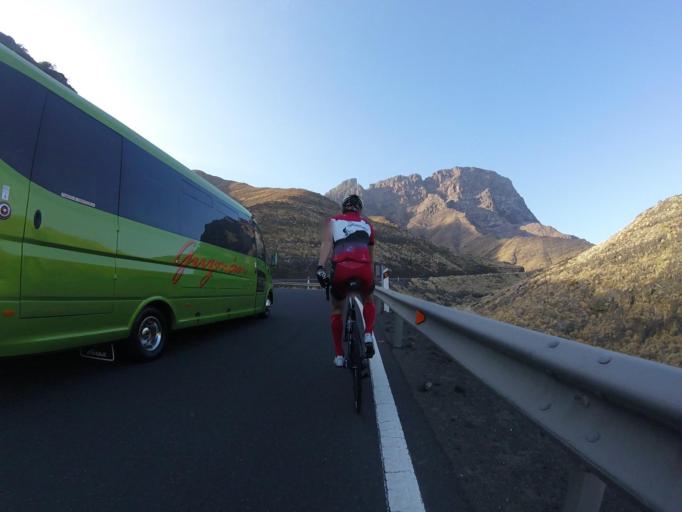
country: ES
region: Canary Islands
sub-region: Provincia de Las Palmas
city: Agaete
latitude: 28.0762
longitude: -15.7087
